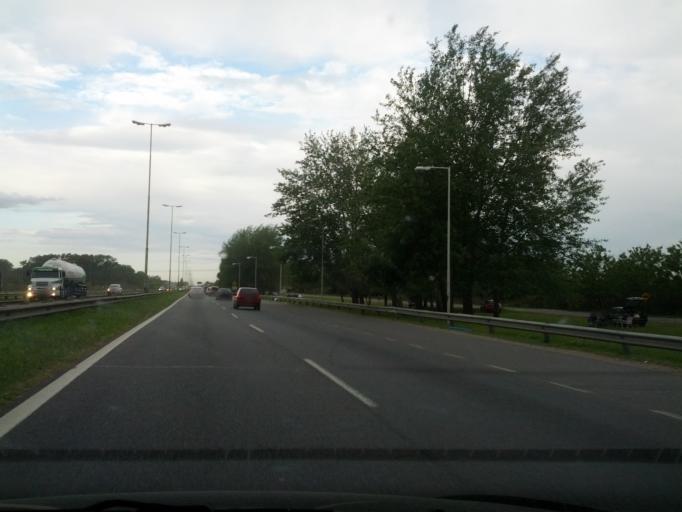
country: AR
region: Buenos Aires
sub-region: Partido de General Rodriguez
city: General Rodriguez
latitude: -34.5861
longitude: -58.9802
